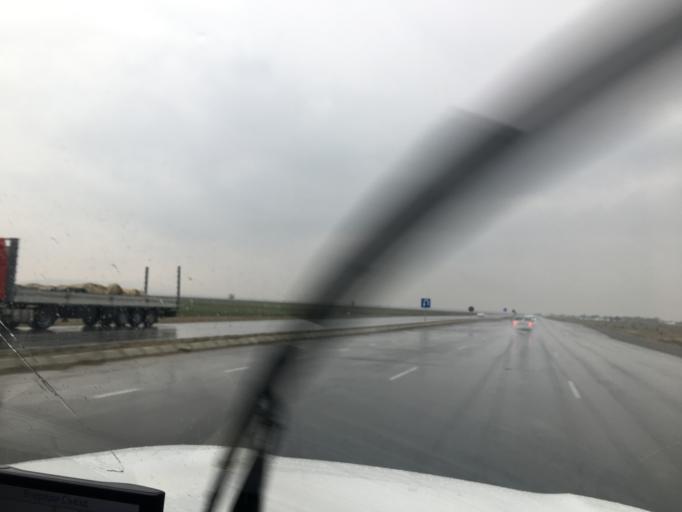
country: TM
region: Ahal
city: Annau
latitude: 37.8202
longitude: 58.7659
